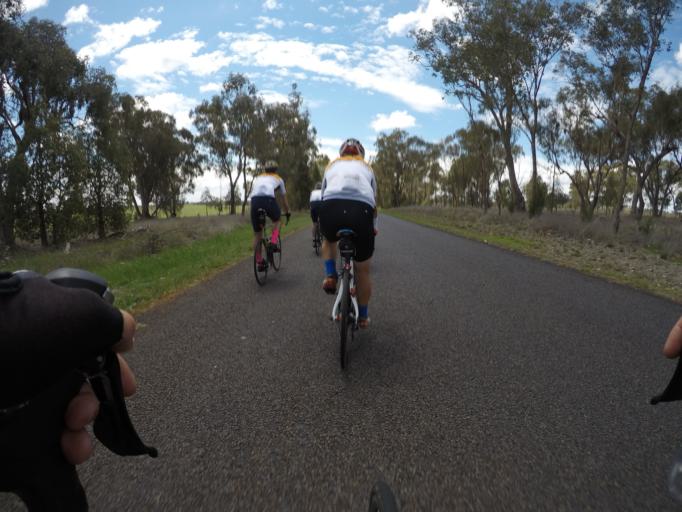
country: AU
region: New South Wales
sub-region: Dubbo Municipality
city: Dubbo
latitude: -32.3644
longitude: 148.5853
